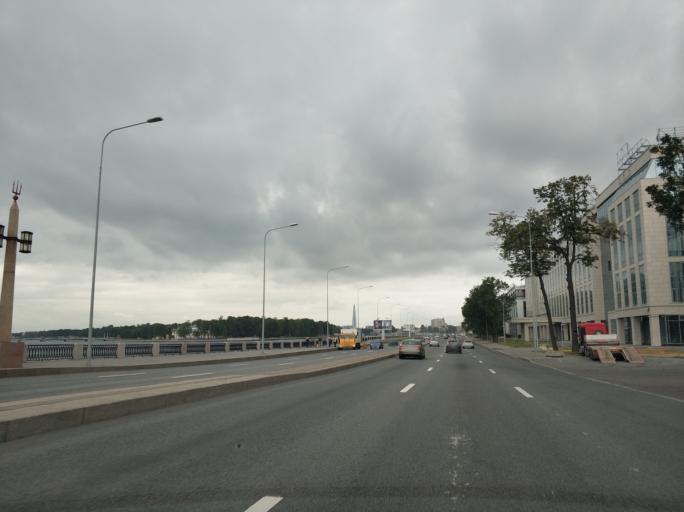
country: RU
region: Leningrad
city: Chernaya Rechka
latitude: 59.9811
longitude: 30.3170
